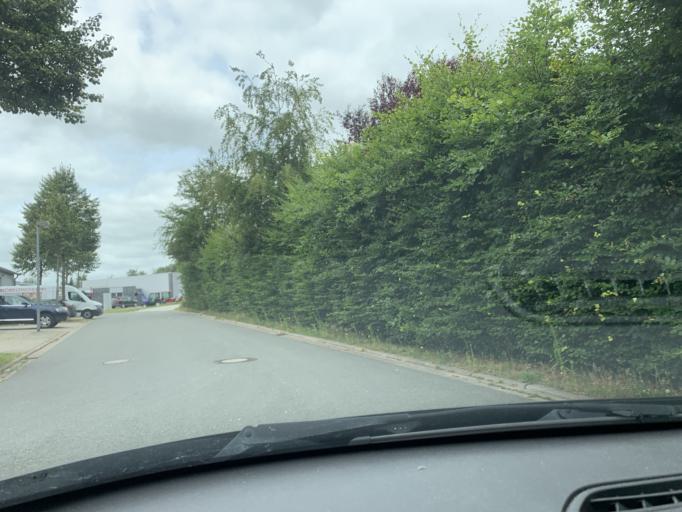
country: DE
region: Lower Saxony
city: Westerstede
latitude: 53.2678
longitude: 7.9531
